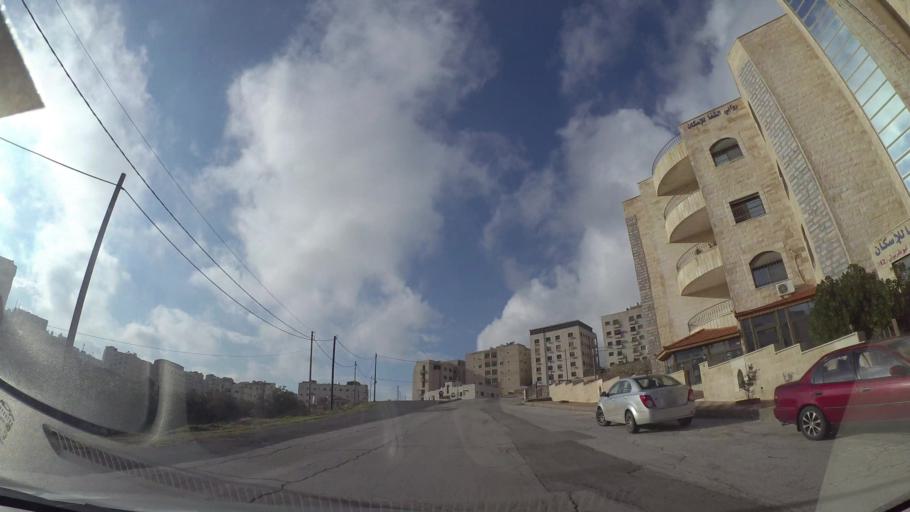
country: JO
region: Amman
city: Al Jubayhah
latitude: 32.0564
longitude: 35.8958
